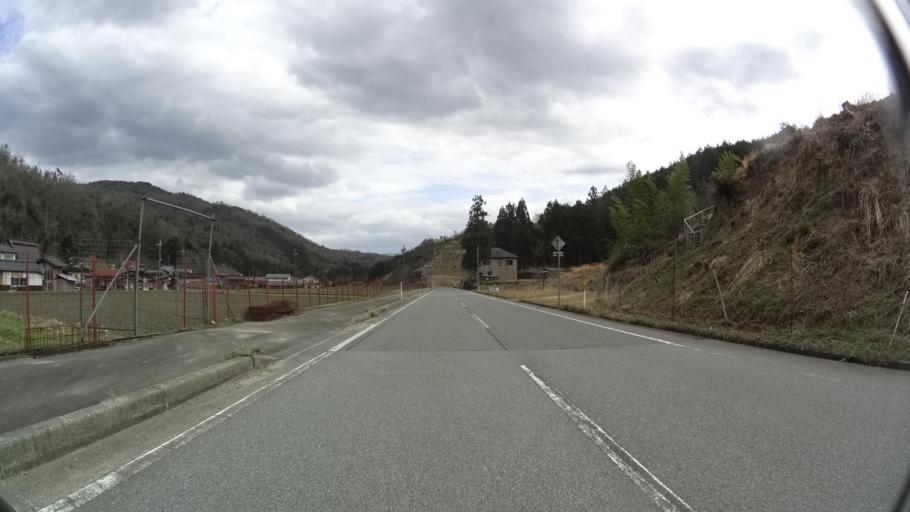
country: JP
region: Hyogo
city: Toyooka
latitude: 35.4861
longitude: 134.9230
